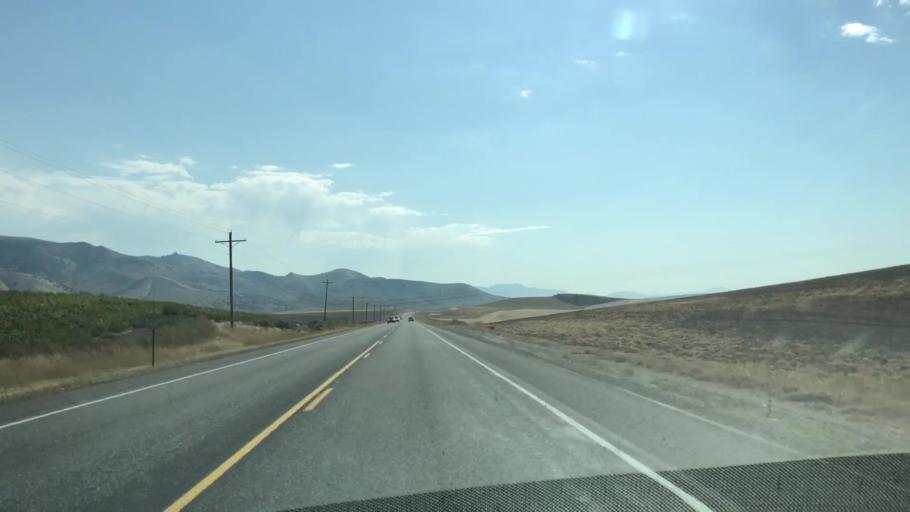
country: US
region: Idaho
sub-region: Madison County
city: Rexburg
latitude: 43.6087
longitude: -111.6800
